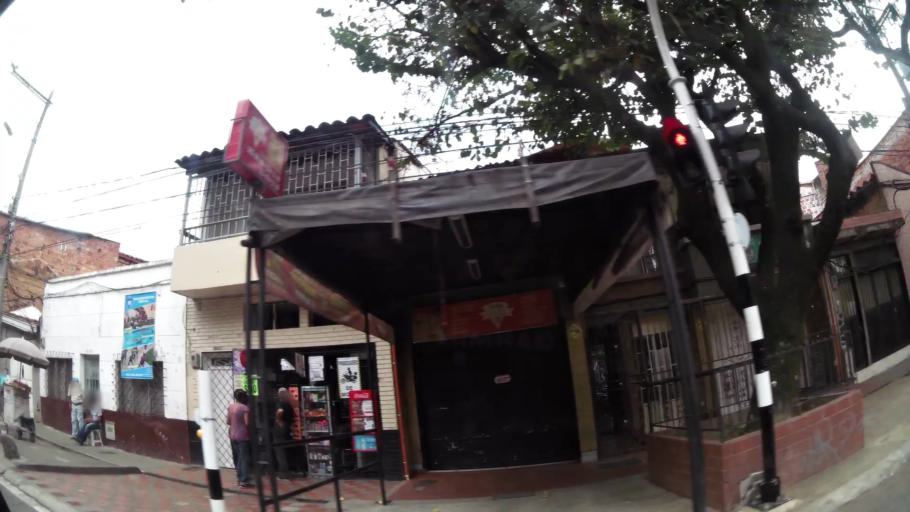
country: CO
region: Antioquia
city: Medellin
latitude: 6.2497
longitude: -75.5551
